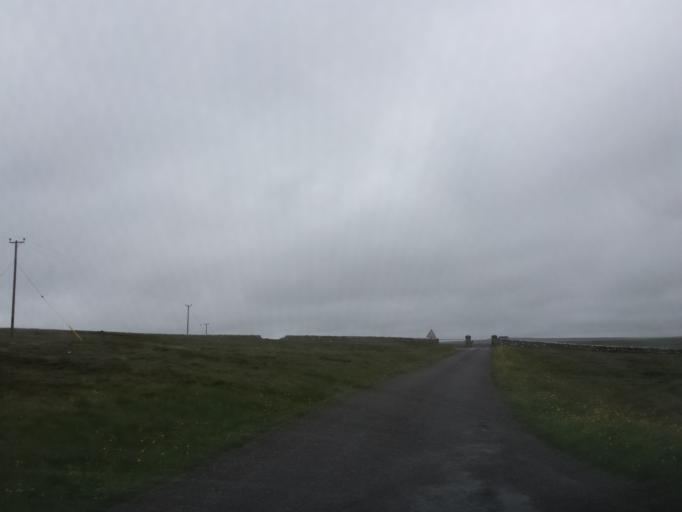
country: GB
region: Scotland
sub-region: Highland
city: Thurso
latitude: 58.6702
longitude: -3.3765
